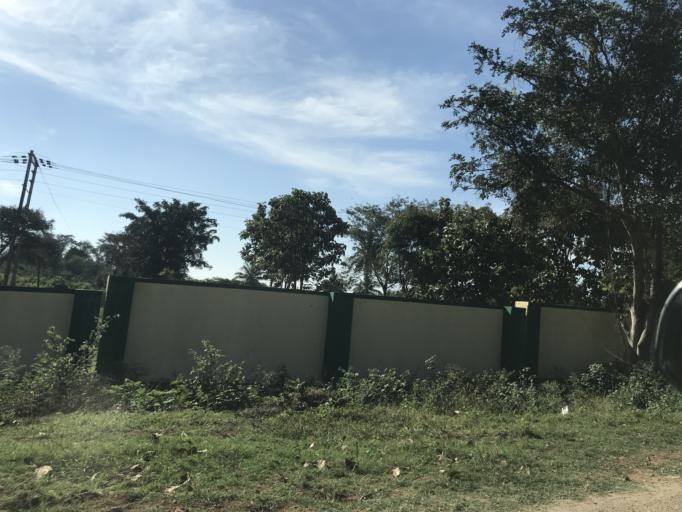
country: IN
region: Karnataka
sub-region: Mysore
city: Mysore
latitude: 12.2089
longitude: 76.5580
